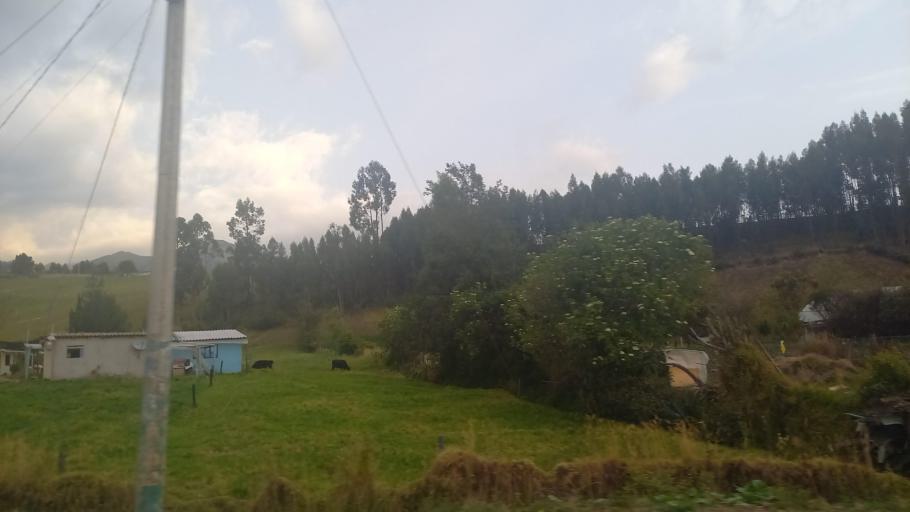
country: EC
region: Pichincha
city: Cayambe
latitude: 0.0853
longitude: -78.1026
